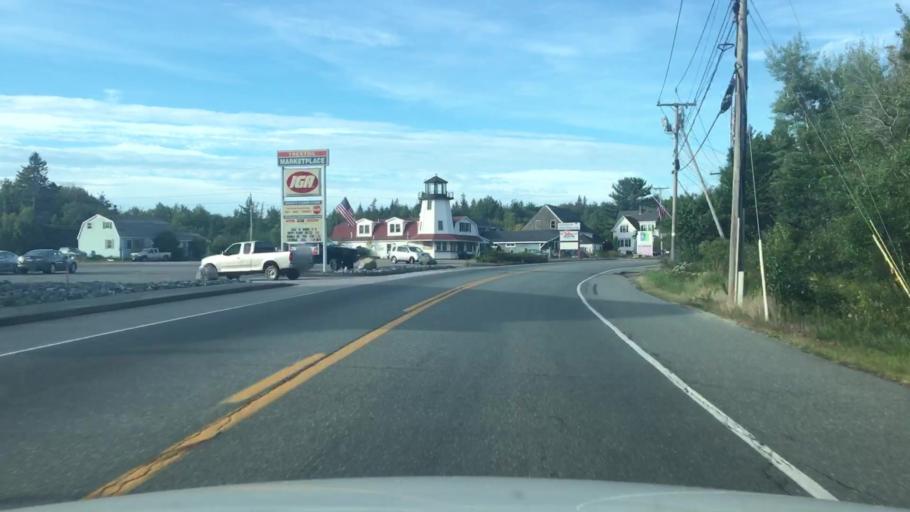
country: US
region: Maine
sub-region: Hancock County
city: Trenton
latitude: 44.4482
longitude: -68.3695
